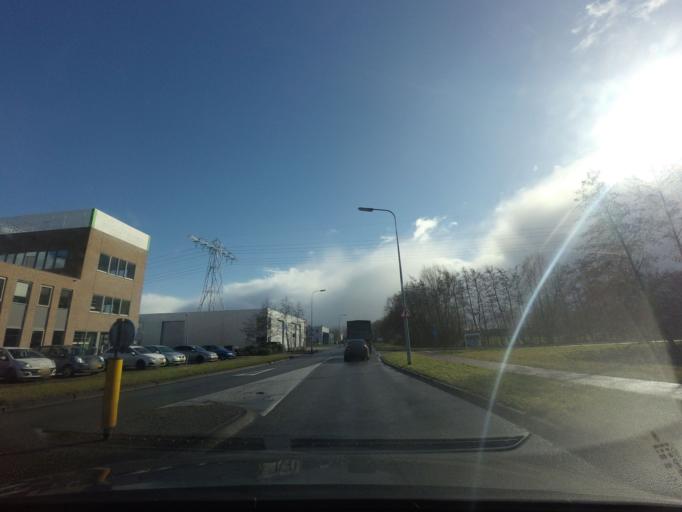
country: NL
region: Groningen
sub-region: Gemeente Groningen
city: Oosterpark
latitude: 53.2142
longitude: 6.6049
